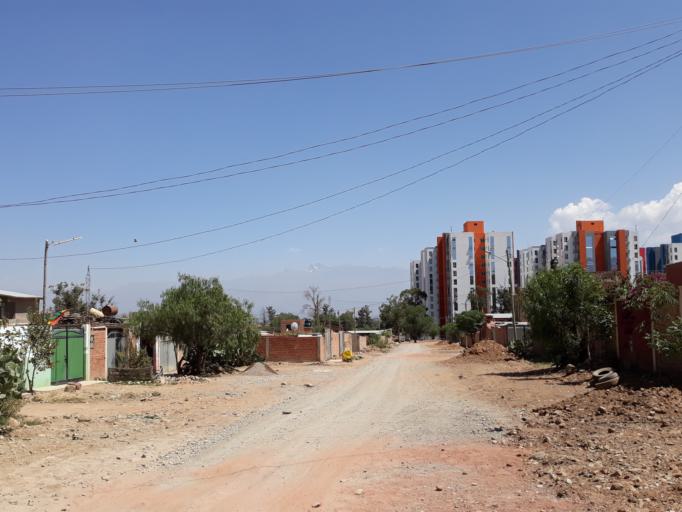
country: BO
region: Cochabamba
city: Cochabamba
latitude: -17.4669
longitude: -66.1378
